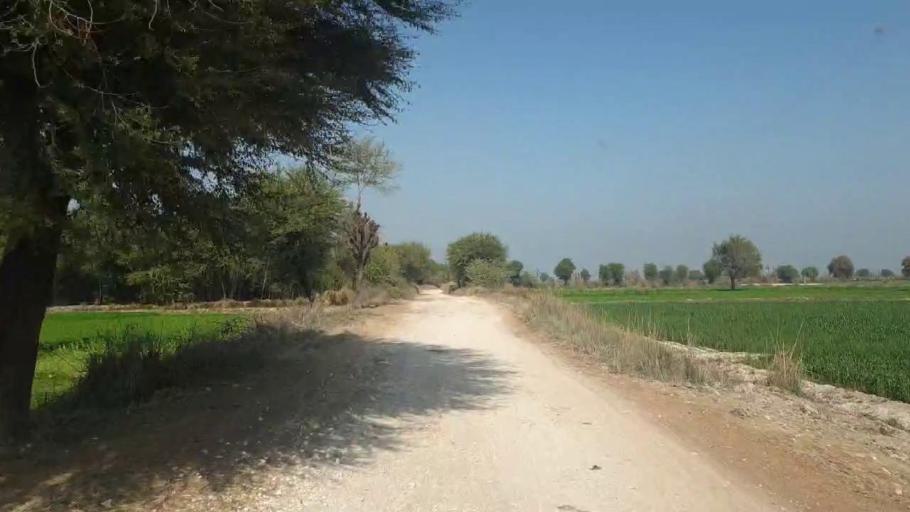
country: PK
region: Sindh
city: Sakrand
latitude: 26.0478
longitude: 68.4338
